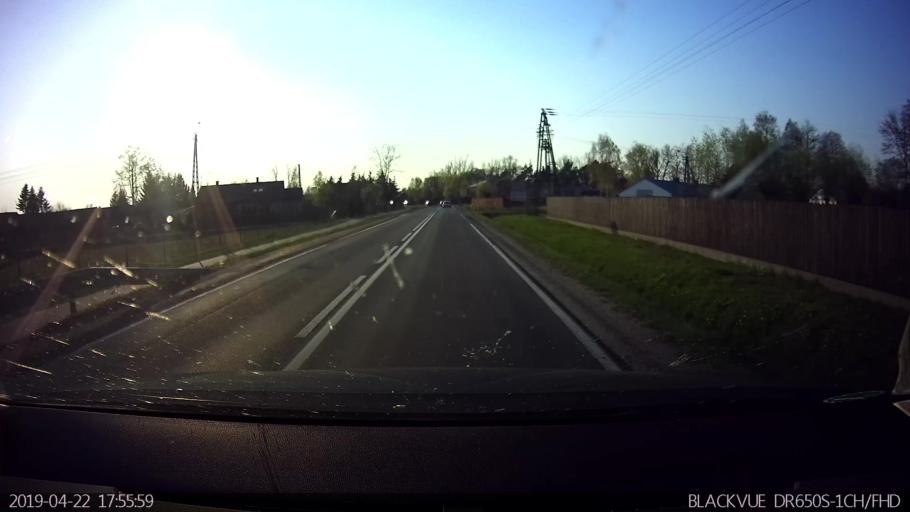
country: PL
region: Masovian Voivodeship
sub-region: Powiat wegrowski
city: Korytnica
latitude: 52.4637
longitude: 21.9132
